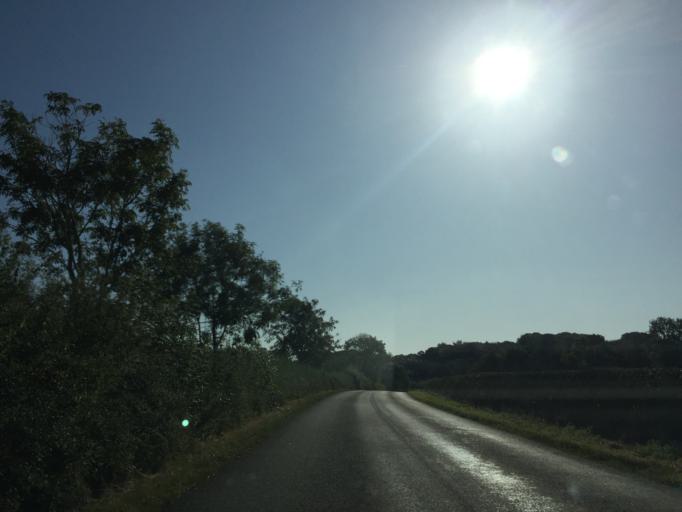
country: GB
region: England
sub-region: Leicestershire
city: Houghton on the Hill
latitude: 52.6380
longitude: -0.9591
